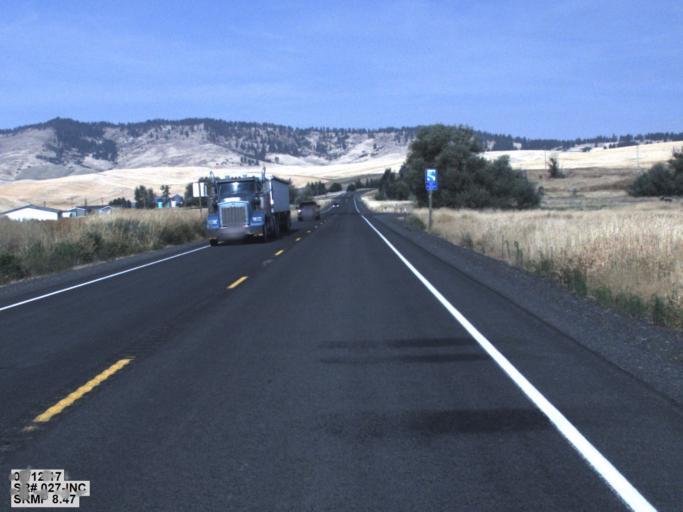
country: US
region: Washington
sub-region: Whitman County
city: Pullman
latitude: 46.8368
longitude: -117.1197
